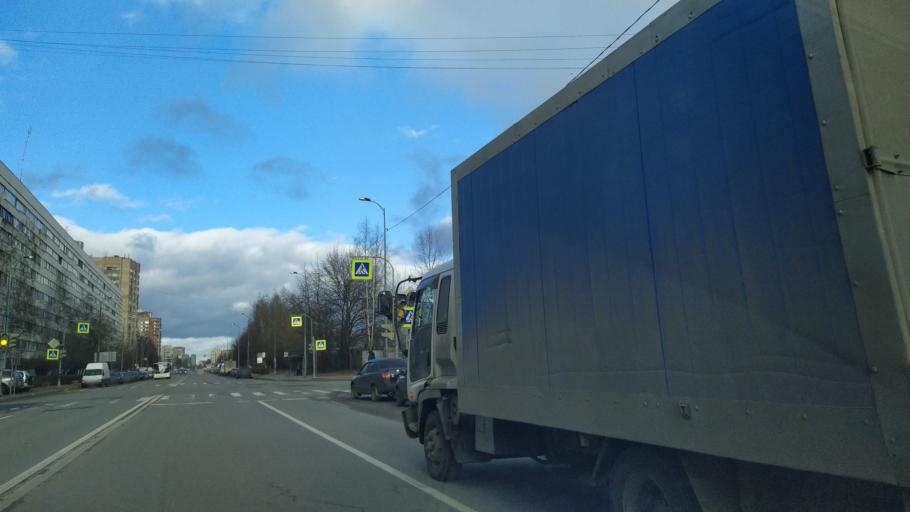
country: RU
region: St.-Petersburg
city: Grazhdanka
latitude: 60.0361
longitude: 30.3814
